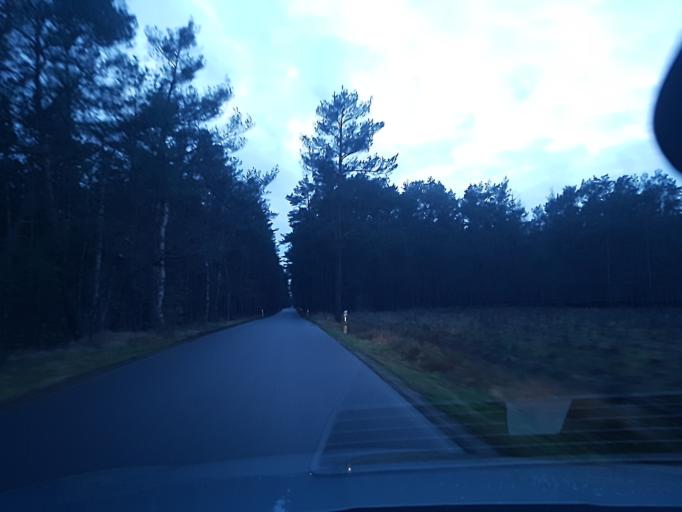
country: DE
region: Brandenburg
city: Ruckersdorf
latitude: 51.5919
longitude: 13.5974
